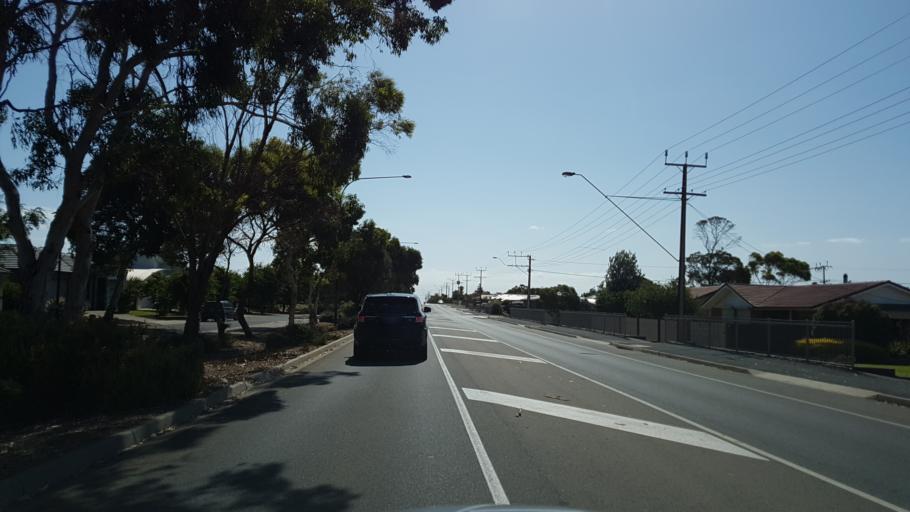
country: AU
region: South Australia
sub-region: Onkaparinga
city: Port Willunga
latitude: -35.2790
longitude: 138.4512
